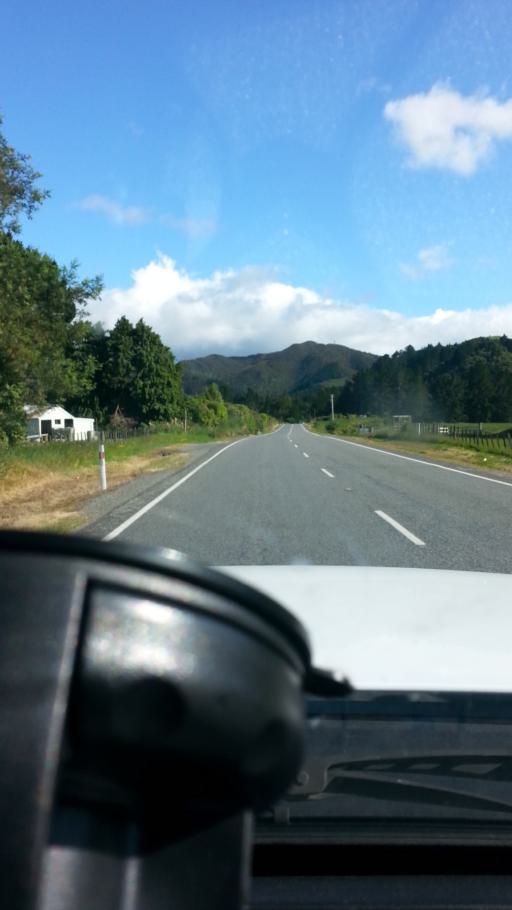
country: NZ
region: Wellington
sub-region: Masterton District
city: Masterton
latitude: -40.7681
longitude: 175.6088
